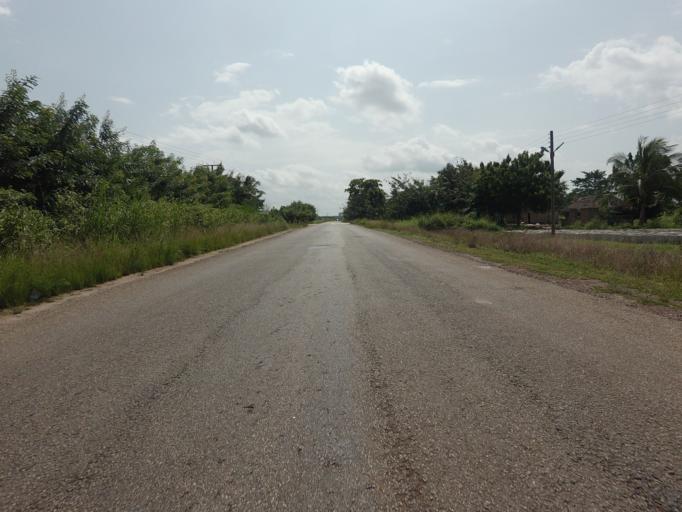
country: TG
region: Maritime
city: Lome
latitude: 6.2558
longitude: 0.9654
